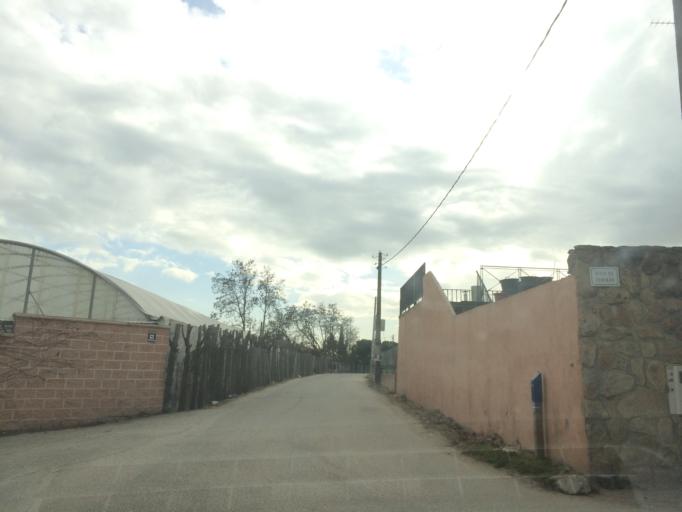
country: ES
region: Madrid
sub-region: Provincia de Madrid
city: Arroyomolinos
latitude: 40.3084
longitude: -3.9463
